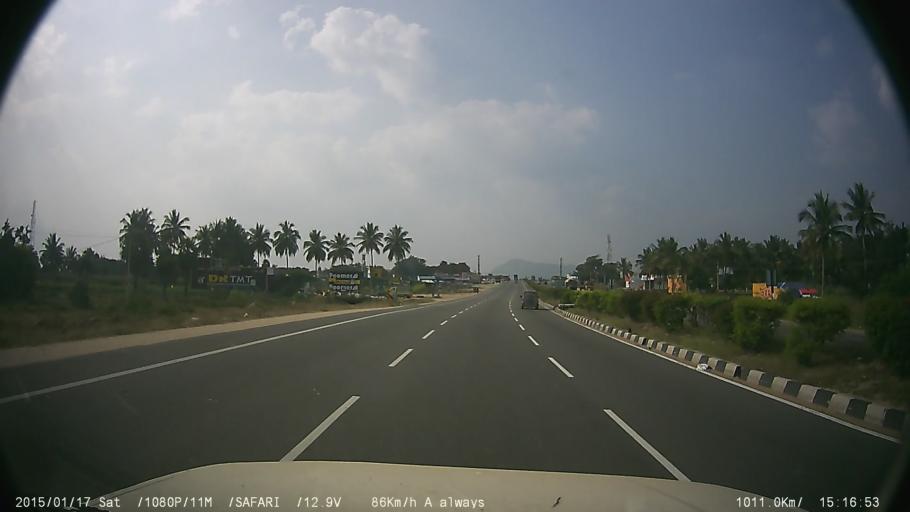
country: IN
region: Tamil Nadu
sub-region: Krishnagiri
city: Krishnagiri
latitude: 12.5774
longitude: 78.1644
